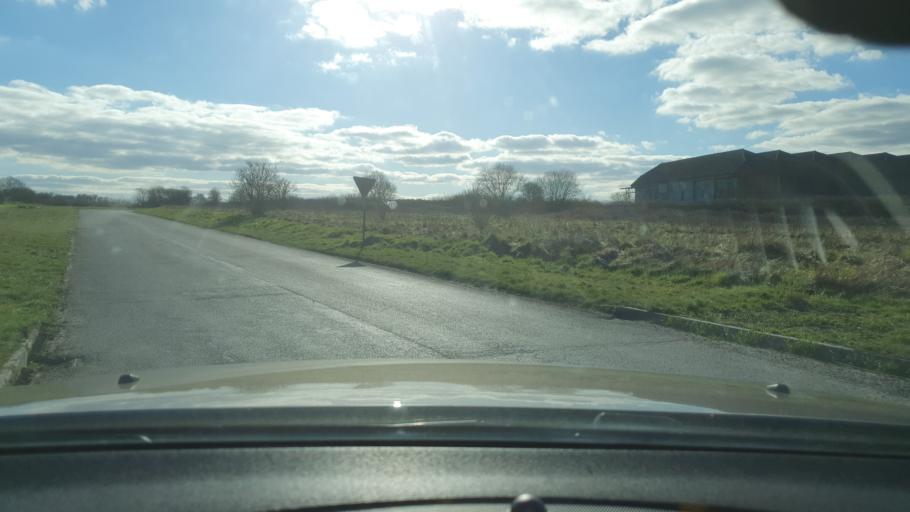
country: GB
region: England
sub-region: Borough of Swindon
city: Wroughton
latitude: 51.5095
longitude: -1.7902
